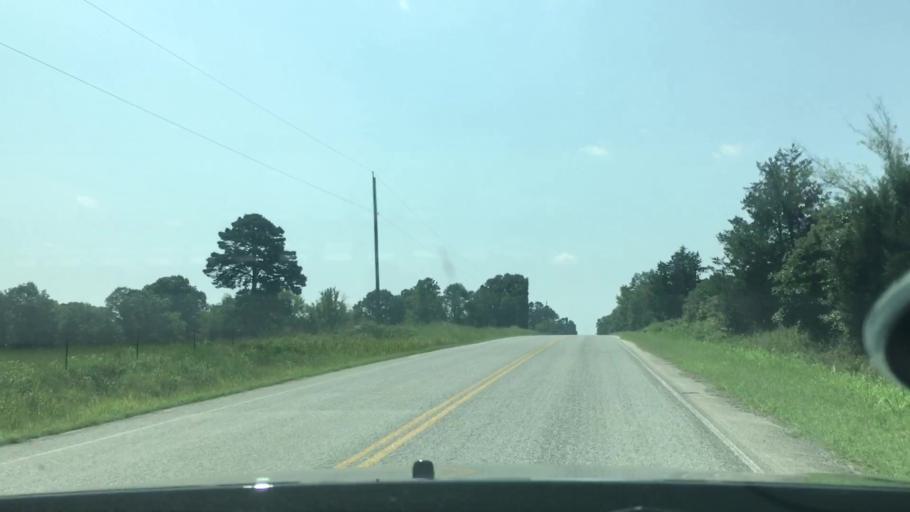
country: US
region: Oklahoma
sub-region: Atoka County
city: Atoka
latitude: 34.2703
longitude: -95.9361
